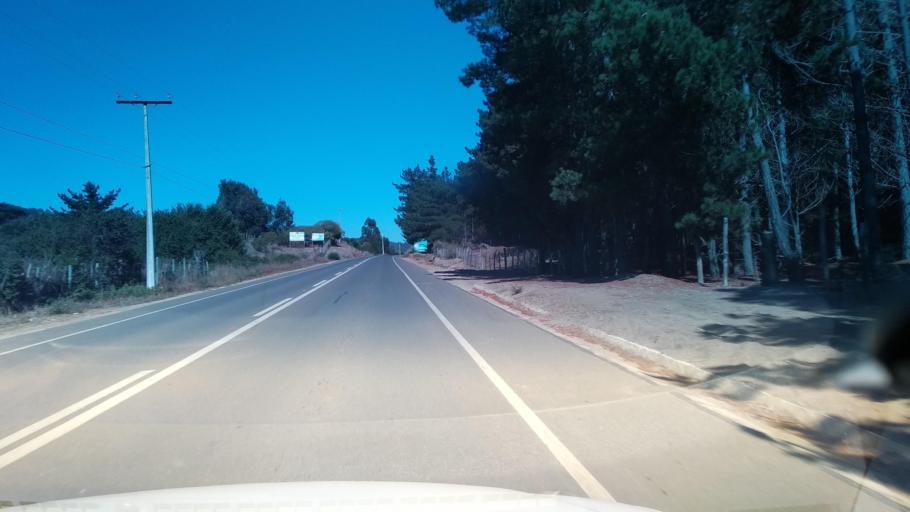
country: CL
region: O'Higgins
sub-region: Provincia de Colchagua
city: Santa Cruz
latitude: -34.4547
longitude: -72.0275
